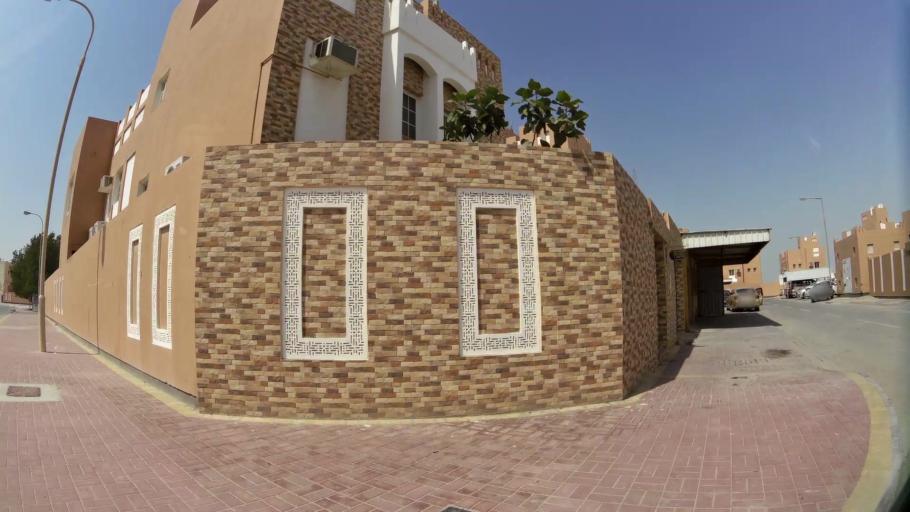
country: BH
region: Manama
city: Jidd Hafs
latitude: 26.2184
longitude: 50.4491
